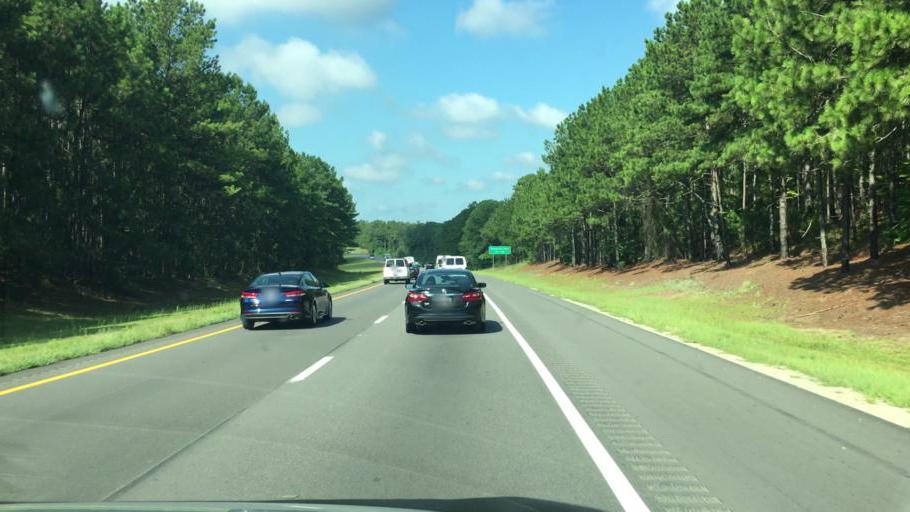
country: US
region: North Carolina
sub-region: Cumberland County
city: Hope Mills
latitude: 34.9693
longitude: -78.8780
